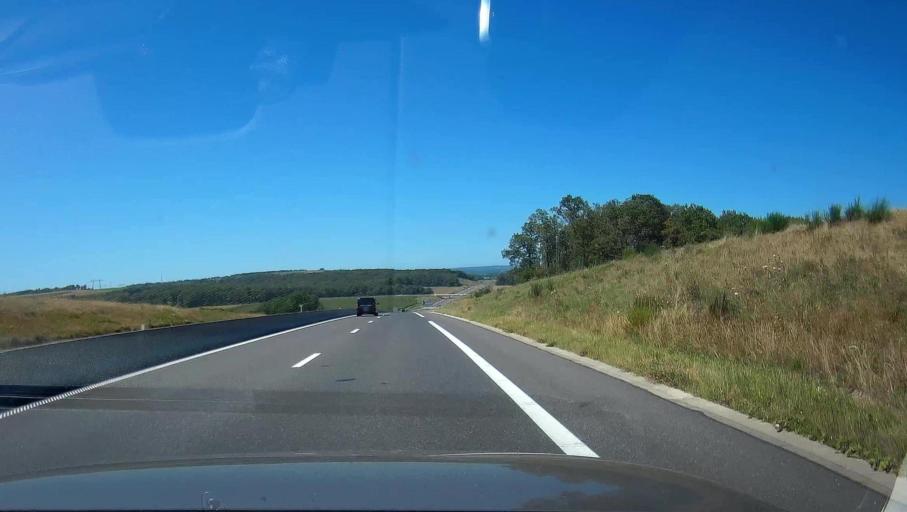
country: FR
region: Champagne-Ardenne
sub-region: Departement des Ardennes
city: Prix-les-Mezieres
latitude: 49.7462
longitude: 4.6697
